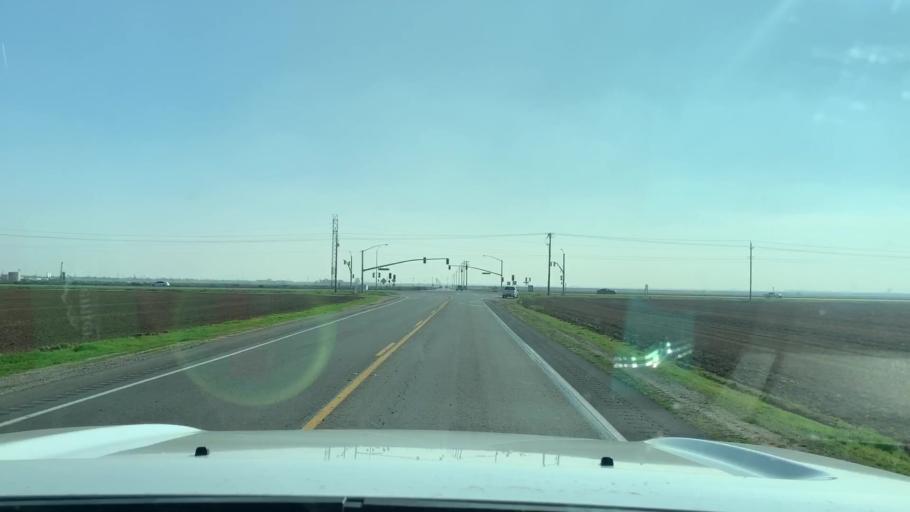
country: US
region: California
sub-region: Kern County
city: Rosedale
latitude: 35.4433
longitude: -119.1543
